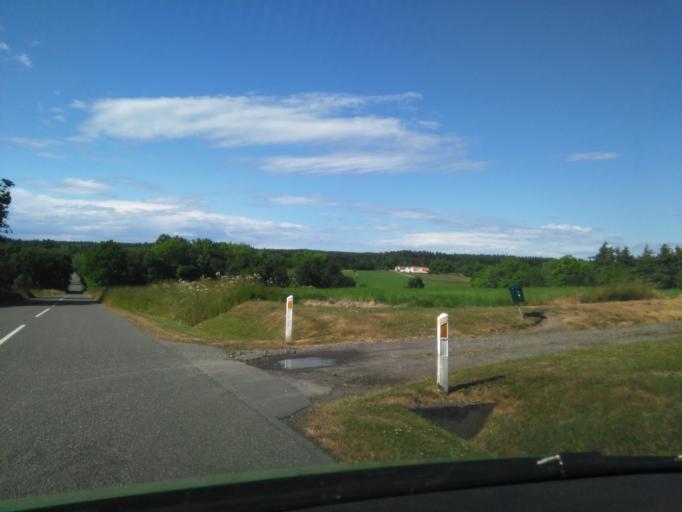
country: DK
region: Capital Region
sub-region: Bornholm Kommune
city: Nexo
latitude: 55.0741
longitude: 15.0809
